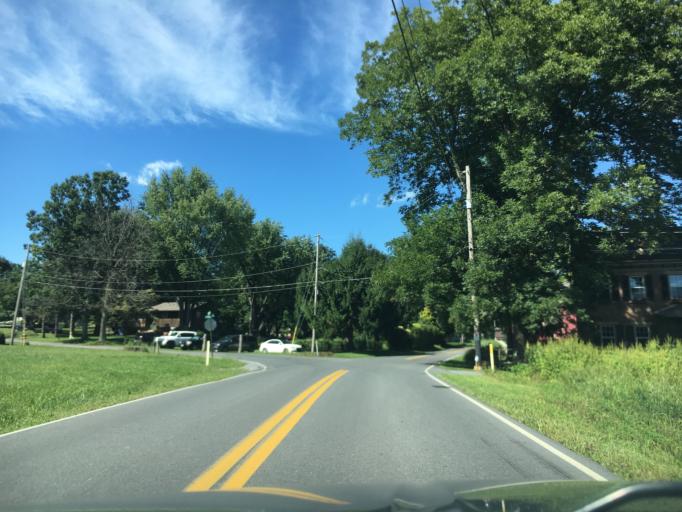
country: US
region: Pennsylvania
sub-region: Berks County
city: Topton
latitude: 40.5162
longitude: -75.6895
